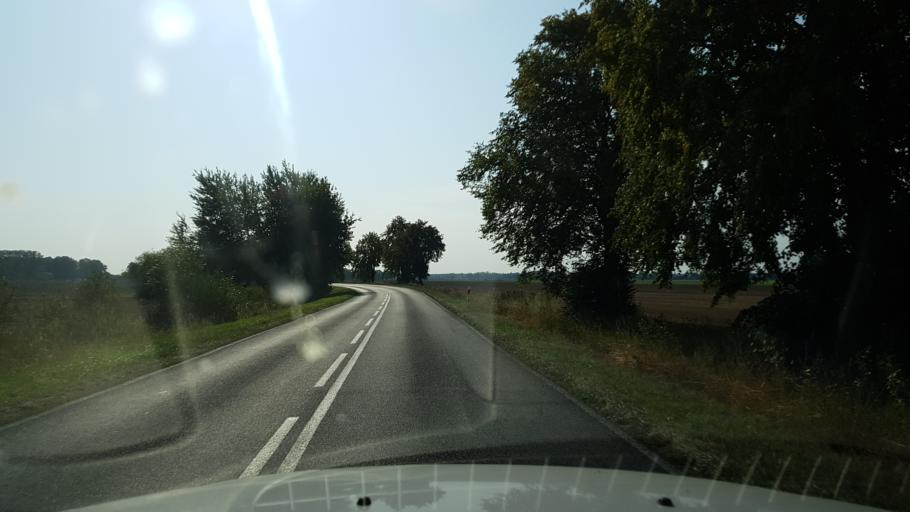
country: PL
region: West Pomeranian Voivodeship
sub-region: Powiat gryficki
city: Ploty
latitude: 53.7929
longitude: 15.2852
